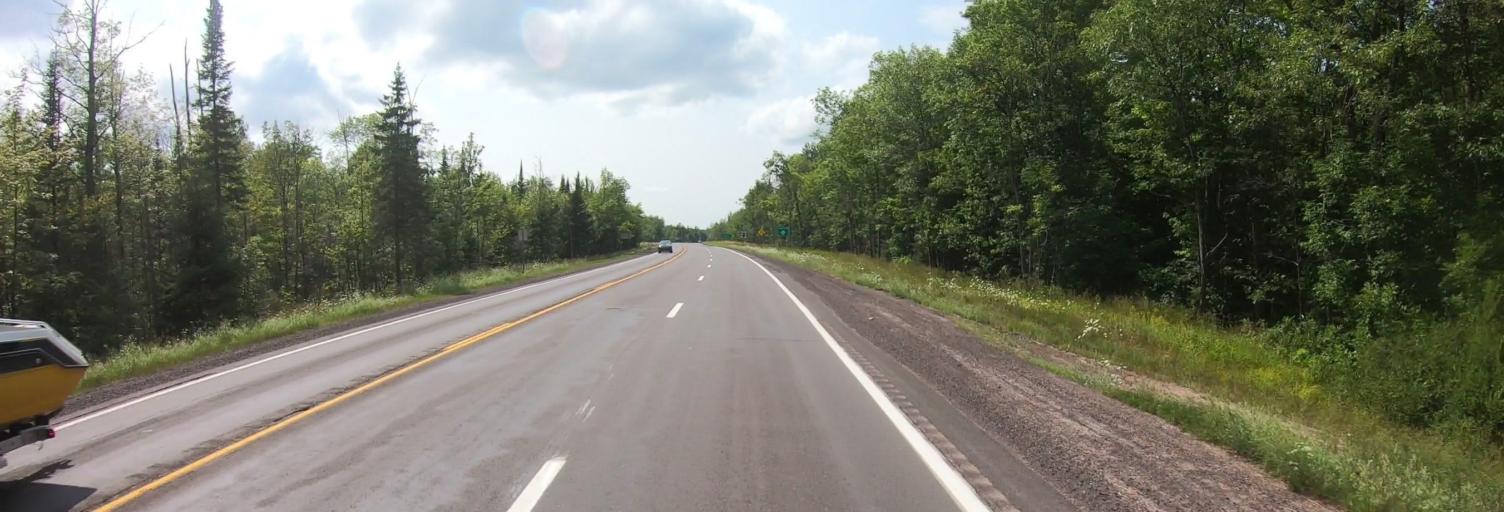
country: US
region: Michigan
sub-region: Ontonagon County
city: Ontonagon
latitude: 46.7793
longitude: -89.0673
